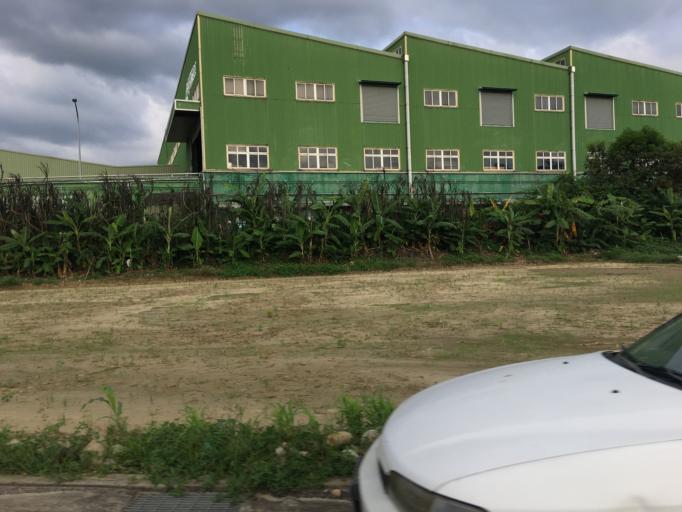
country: TW
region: Taiwan
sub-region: Taichung City
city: Taichung
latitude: 24.0919
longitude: 120.7118
